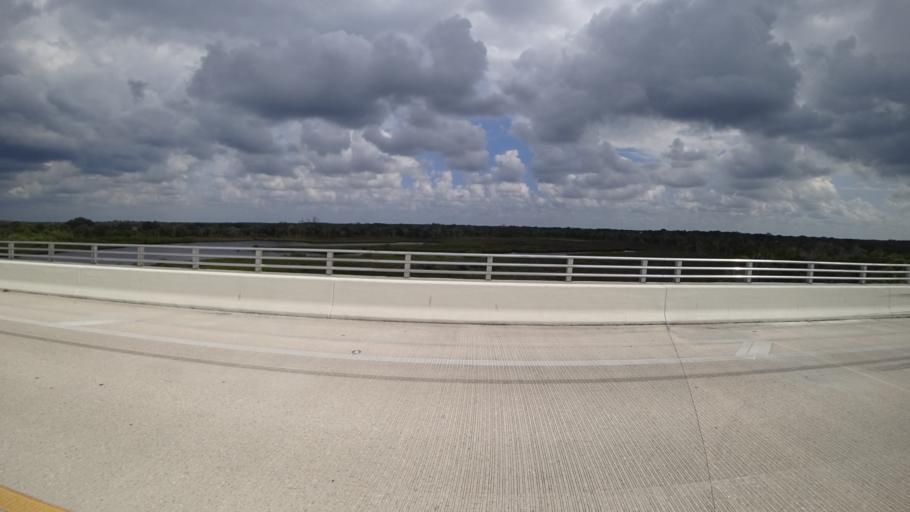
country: US
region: Florida
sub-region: Manatee County
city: Ellenton
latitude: 27.5210
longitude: -82.4285
